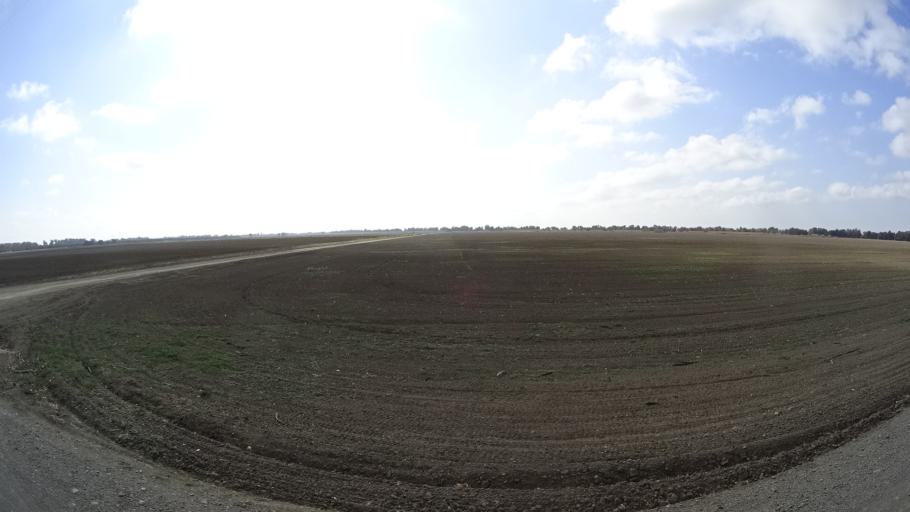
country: US
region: California
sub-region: Yolo County
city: Woodland
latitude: 38.7957
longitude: -121.7102
